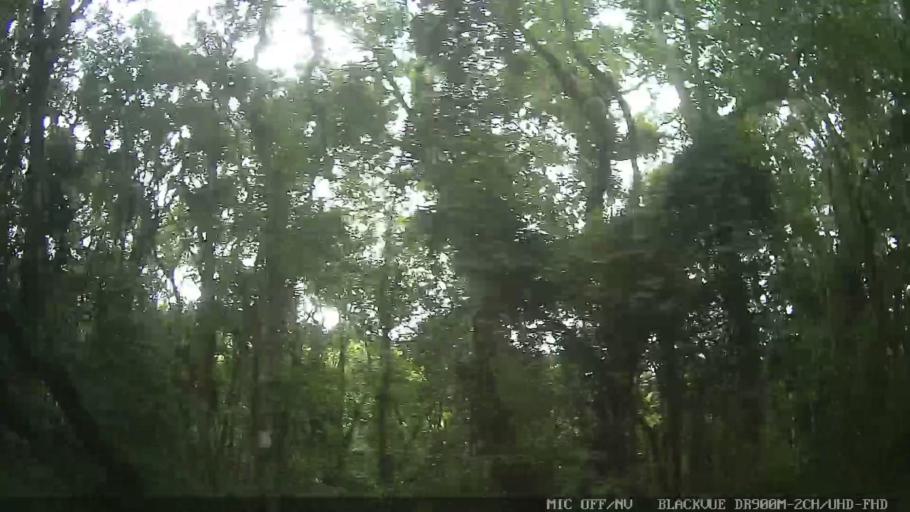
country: BR
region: Sao Paulo
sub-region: Santa Branca
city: Santa Branca
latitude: -23.5538
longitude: -45.6791
